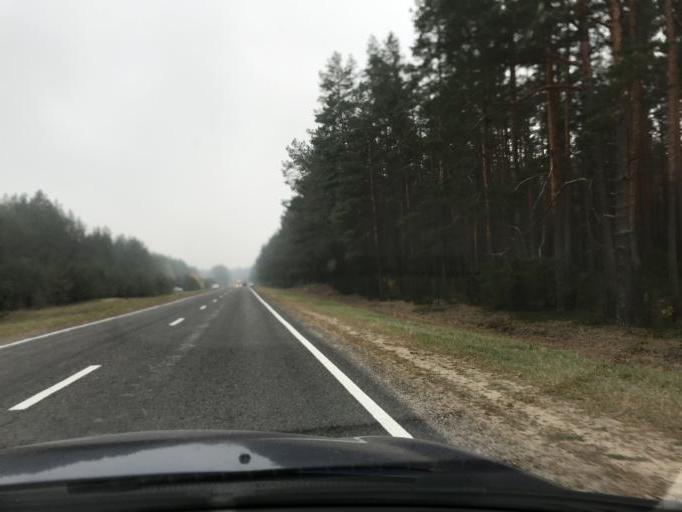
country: LT
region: Alytaus apskritis
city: Druskininkai
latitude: 53.8551
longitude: 23.8918
